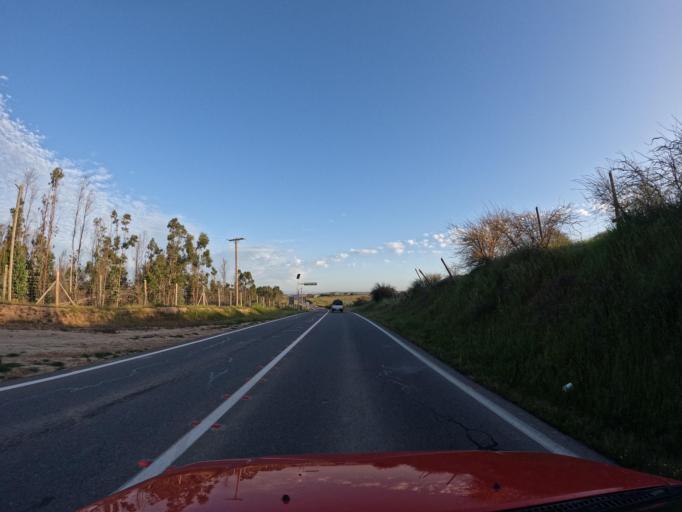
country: CL
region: O'Higgins
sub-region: Provincia de Colchagua
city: Santa Cruz
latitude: -34.2680
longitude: -71.7339
